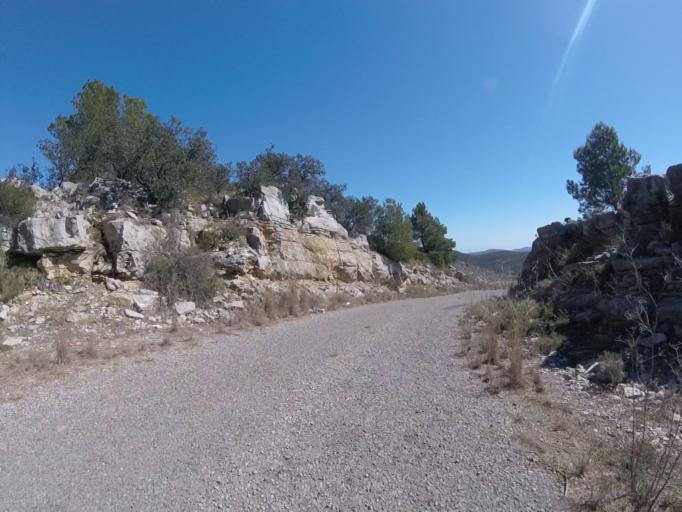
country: ES
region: Valencia
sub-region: Provincia de Castello
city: Cervera del Maestre
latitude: 40.4135
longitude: 0.2027
